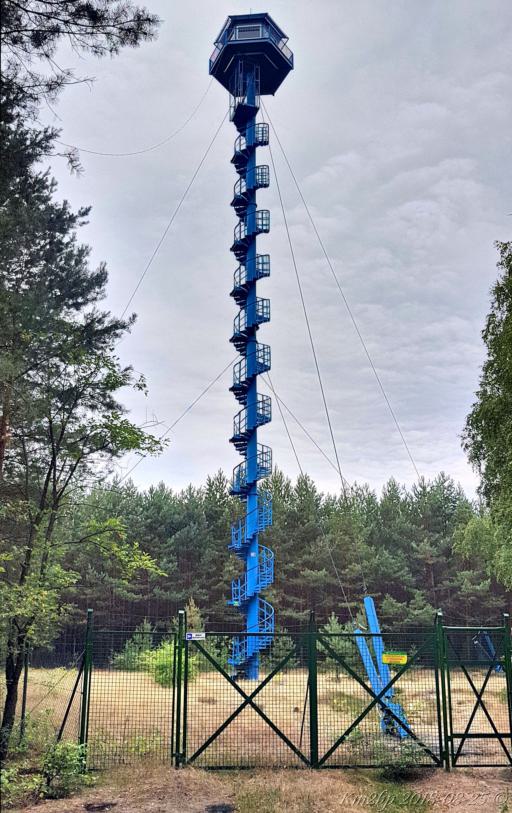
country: PL
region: Lubusz
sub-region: Zielona Gora
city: Zielona Gora
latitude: 51.9533
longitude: 15.6061
